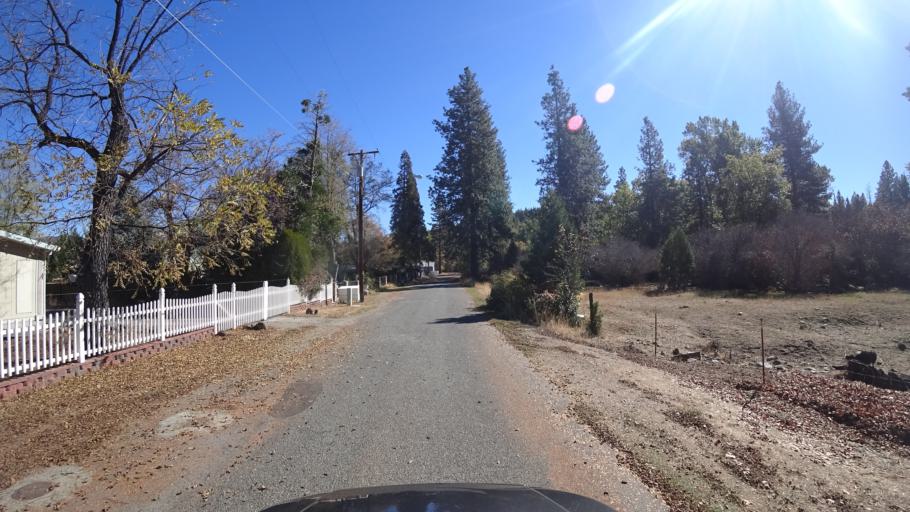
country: US
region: California
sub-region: Siskiyou County
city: Yreka
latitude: 41.4548
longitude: -122.8867
